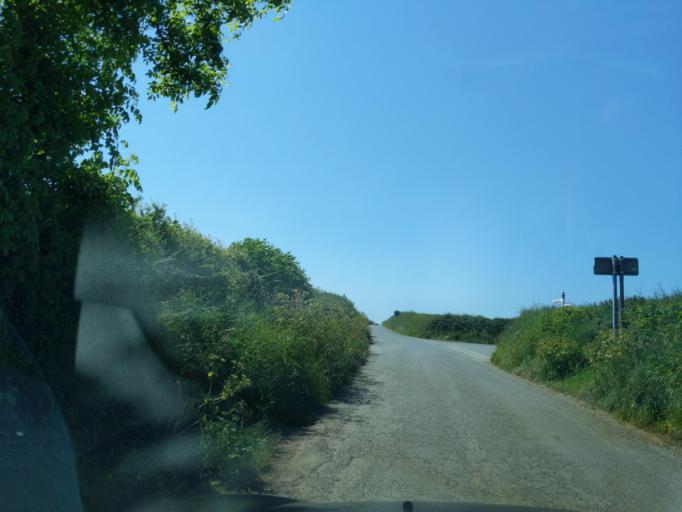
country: GB
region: England
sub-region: Cornwall
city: Wadebridge
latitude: 50.5810
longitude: -4.8349
